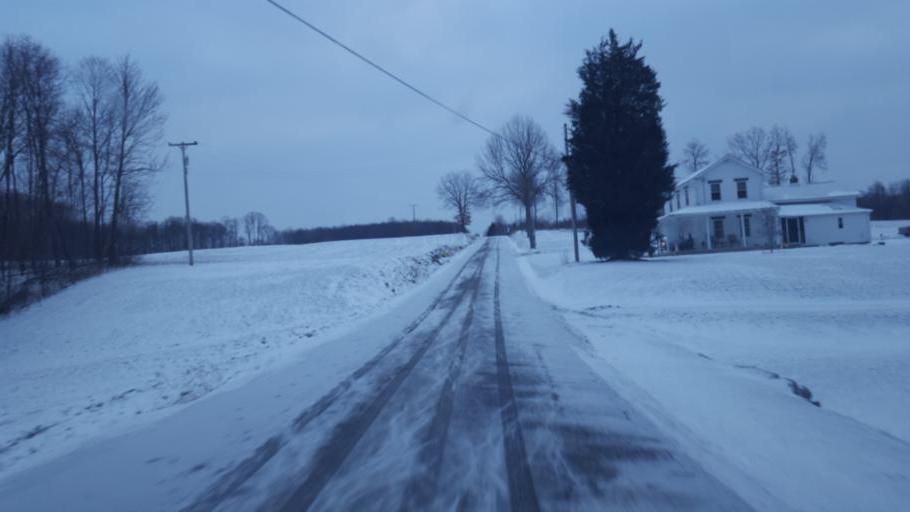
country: US
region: Pennsylvania
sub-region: Crawford County
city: Cochranton
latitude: 41.4329
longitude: -80.0026
